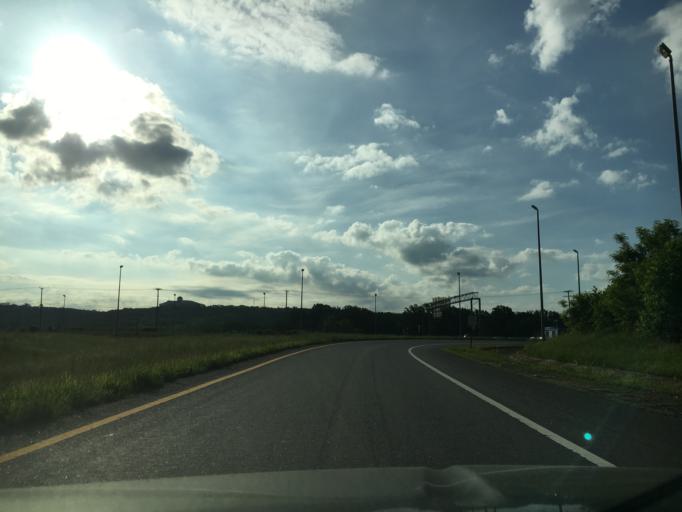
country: US
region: Virginia
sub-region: Campbell County
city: Timberlake
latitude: 37.3375
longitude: -79.1929
